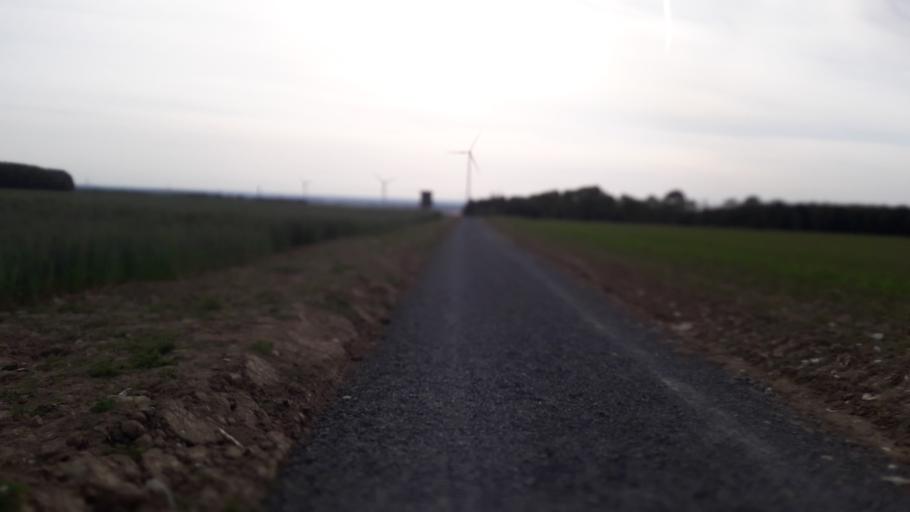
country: DE
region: North Rhine-Westphalia
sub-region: Regierungsbezirk Detmold
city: Paderborn
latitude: 51.6838
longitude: 8.7643
